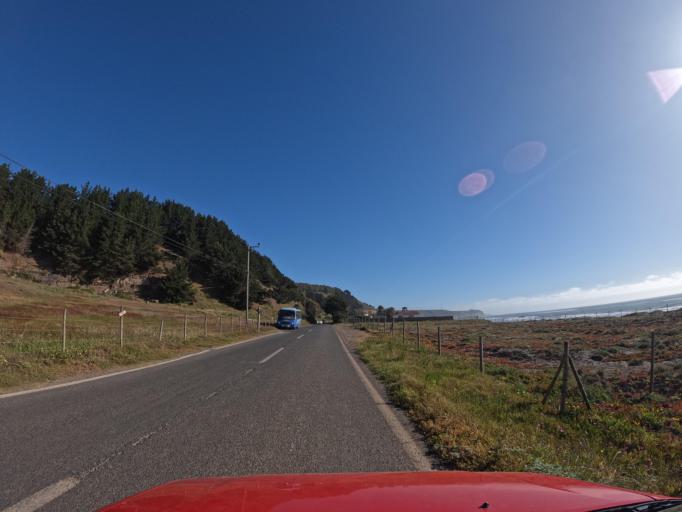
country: CL
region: Maule
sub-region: Provincia de Talca
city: Constitucion
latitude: -34.8656
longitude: -72.1482
